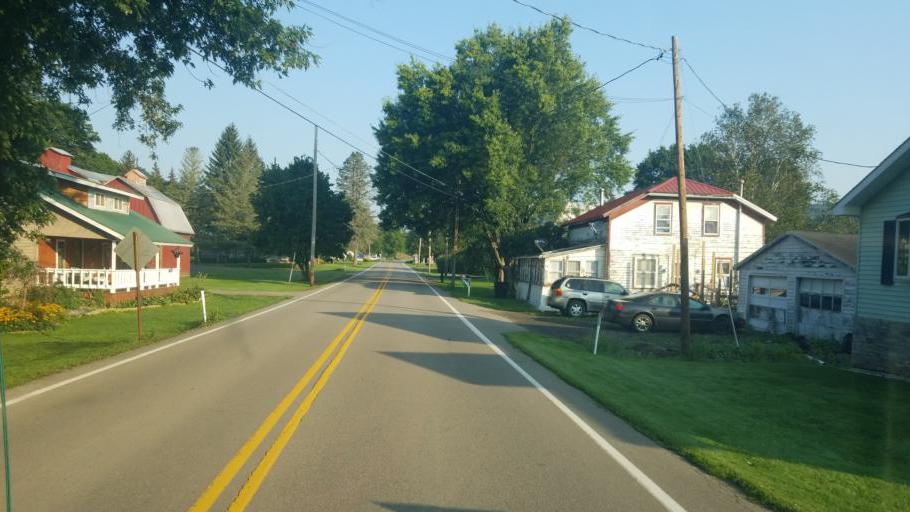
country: US
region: Pennsylvania
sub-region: Tioga County
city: Westfield
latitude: 41.9940
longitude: -77.4963
